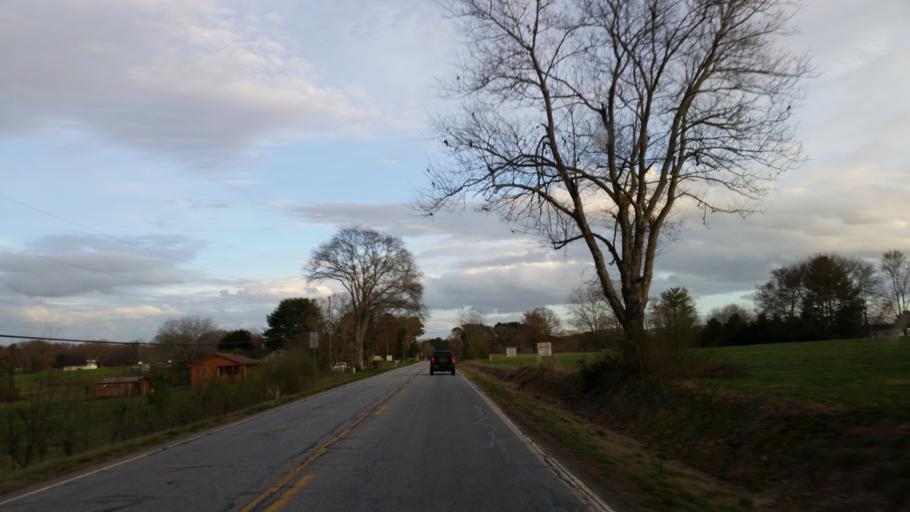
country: US
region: Georgia
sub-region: Pickens County
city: Jasper
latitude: 34.4803
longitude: -84.5825
